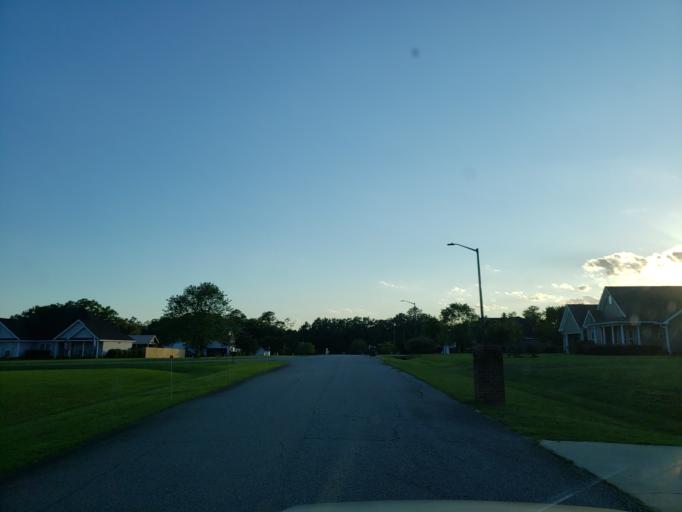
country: US
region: Georgia
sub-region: Lowndes County
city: Valdosta
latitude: 30.7580
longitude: -83.2564
